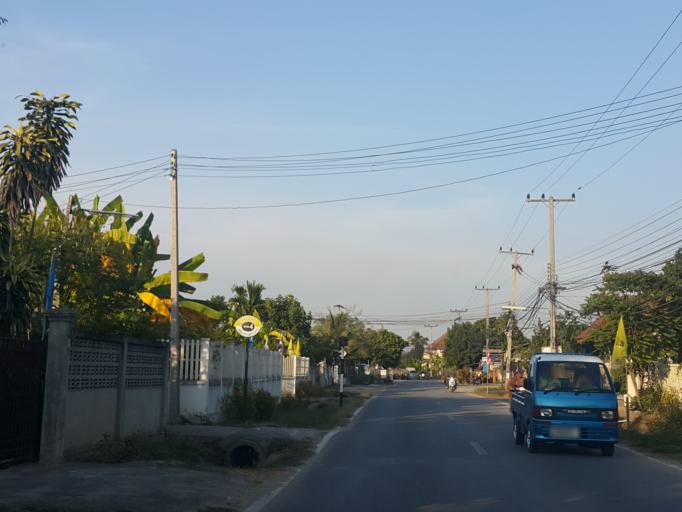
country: TH
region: Chiang Mai
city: San Sai
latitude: 18.8278
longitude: 99.0808
